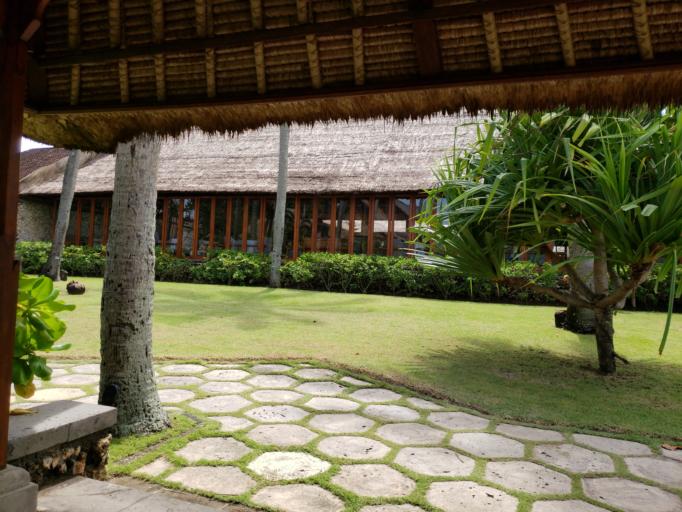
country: ID
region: Bali
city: Kuta
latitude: -8.6885
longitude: 115.1561
